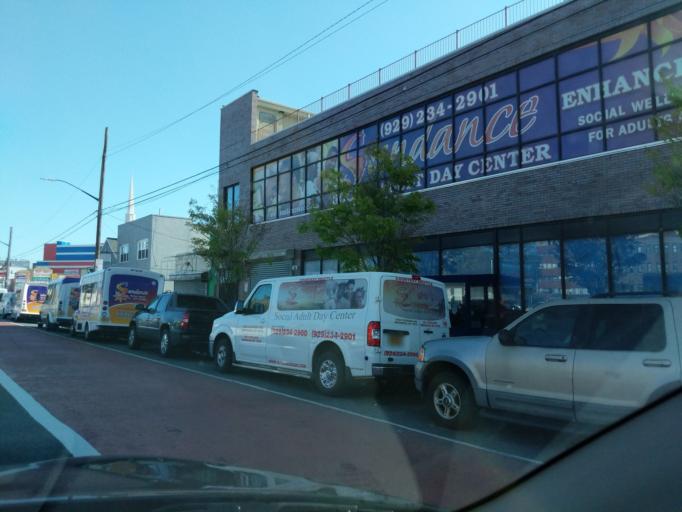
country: US
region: New York
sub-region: Kings County
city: Brooklyn
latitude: 40.6598
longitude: -73.9312
